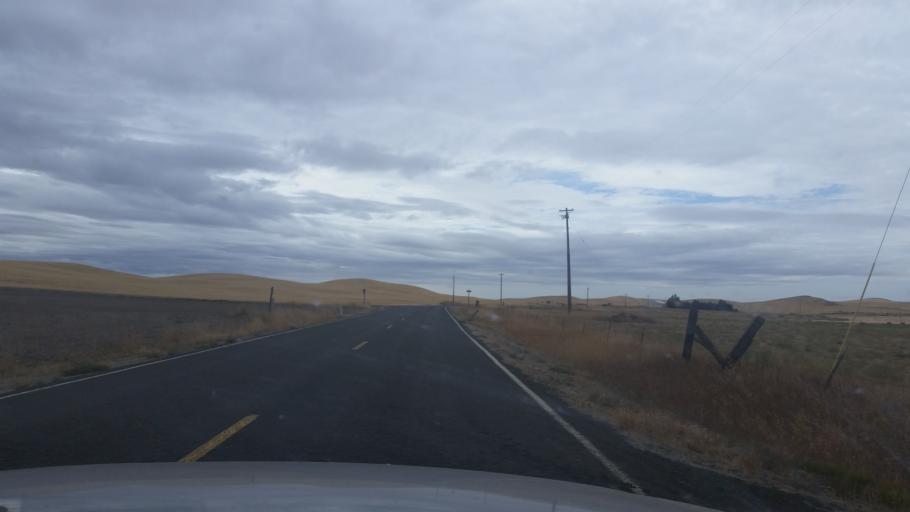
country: US
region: Washington
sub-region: Spokane County
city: Medical Lake
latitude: 47.5184
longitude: -117.8863
